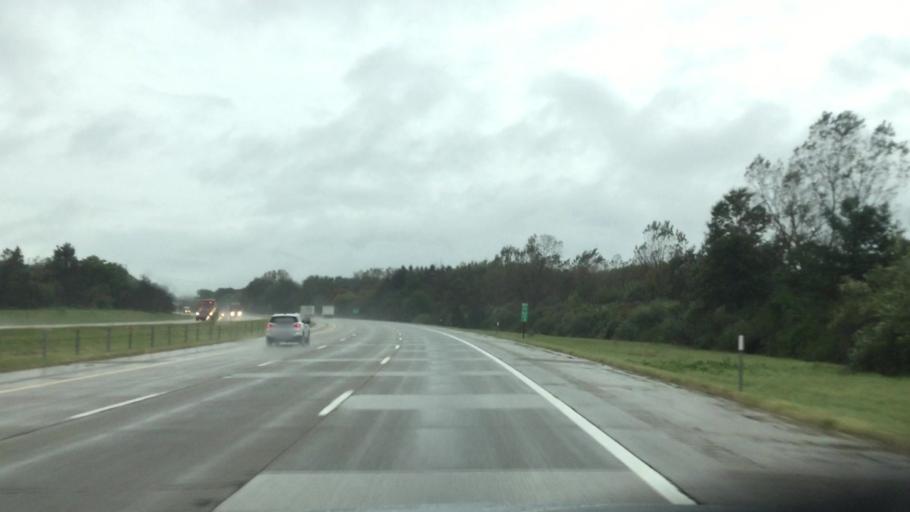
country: US
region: Michigan
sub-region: Berrien County
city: Fair Plain
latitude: 42.0525
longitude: -86.4865
